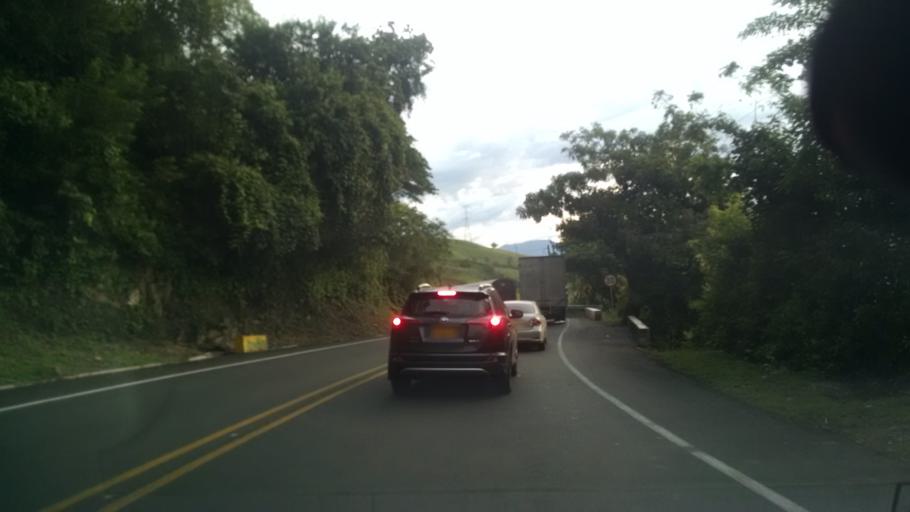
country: CO
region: Antioquia
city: Santa Barbara
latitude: 5.8384
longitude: -75.5841
